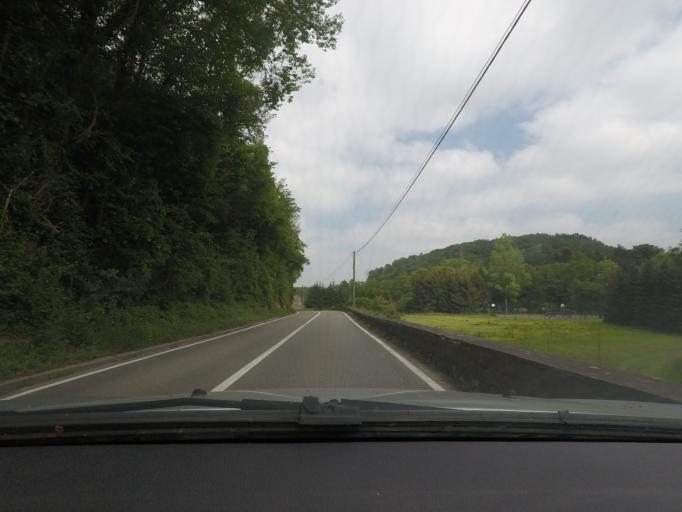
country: BE
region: Wallonia
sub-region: Province de Namur
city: Assesse
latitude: 50.4345
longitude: 5.0030
